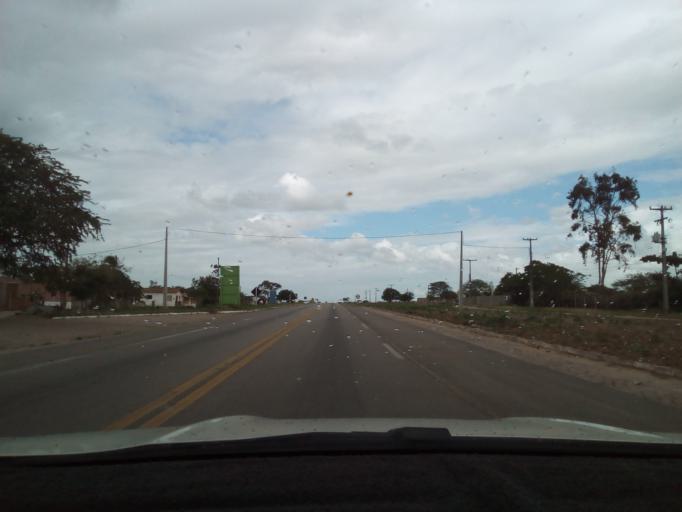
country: BR
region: Rio Grande do Norte
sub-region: Sao Paulo Do Potengi
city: Sao Paulo do Potengi
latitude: -5.8424
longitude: -35.6894
